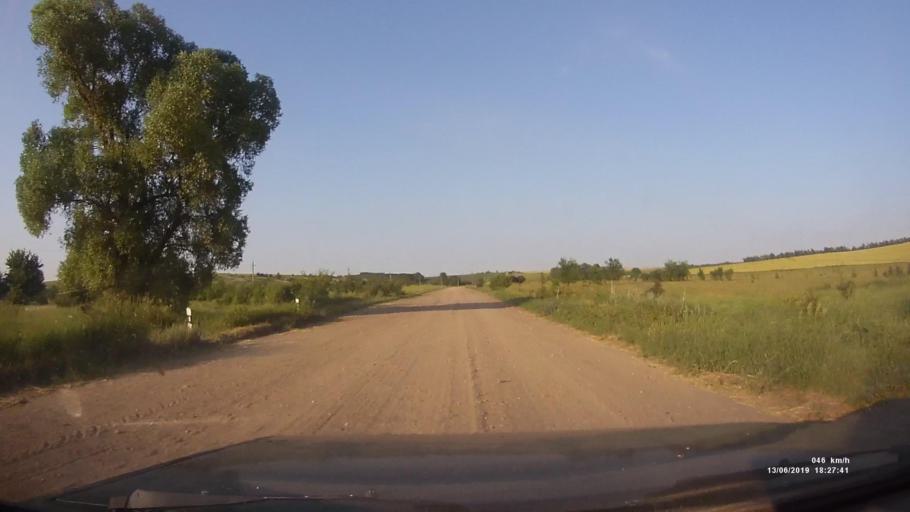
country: RU
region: Rostov
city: Kazanskaya
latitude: 49.8550
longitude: 41.3253
